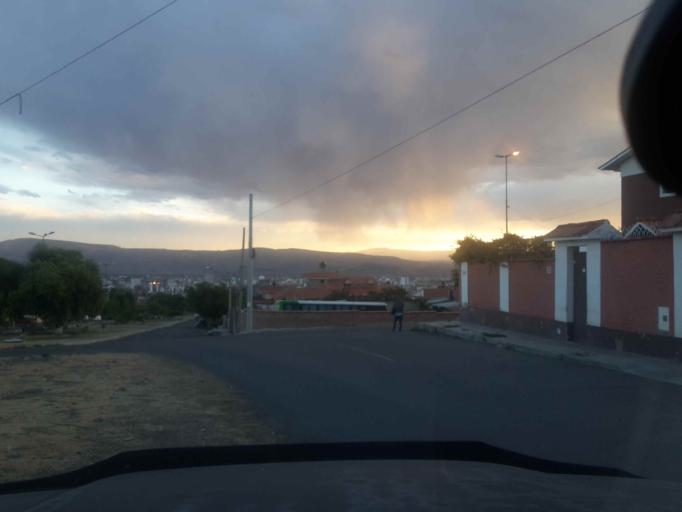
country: BO
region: Cochabamba
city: Cochabamba
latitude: -17.3566
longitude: -66.1689
